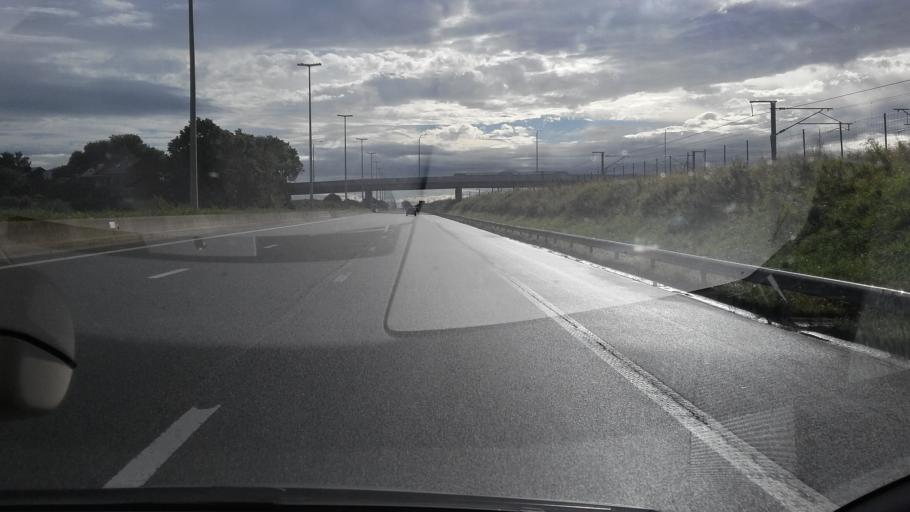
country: BE
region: Wallonia
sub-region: Province de Liege
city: Waremme
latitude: 50.7059
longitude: 5.2691
